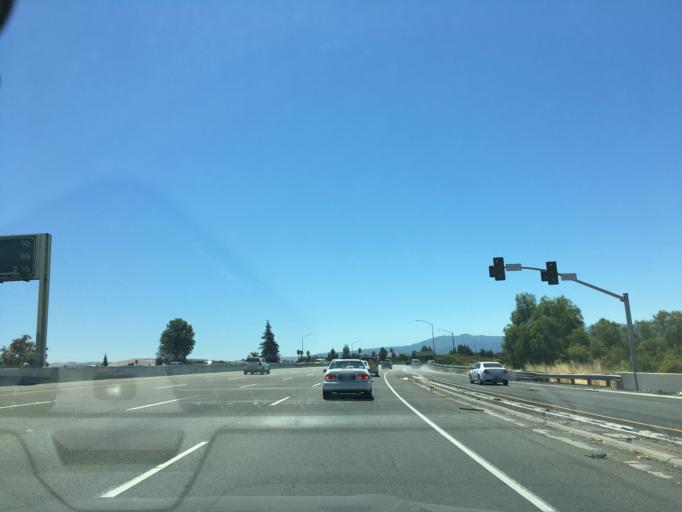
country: US
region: California
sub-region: Santa Clara County
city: Alum Rock
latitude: 37.3541
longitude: -121.8383
